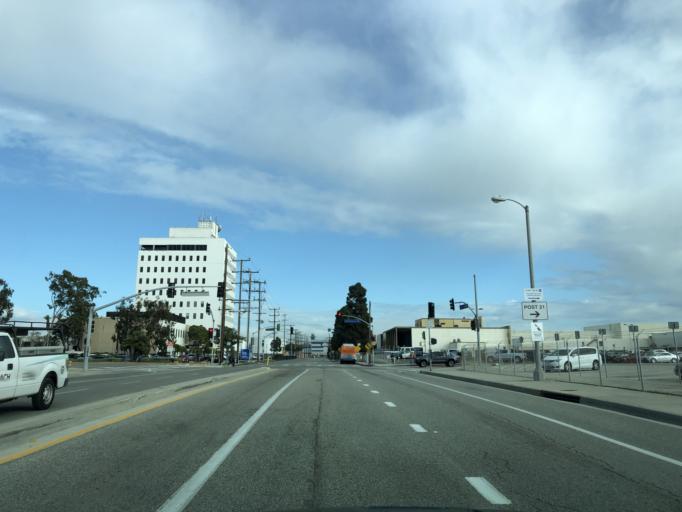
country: US
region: California
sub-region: Los Angeles County
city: El Segundo
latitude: 33.9414
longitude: -118.4255
